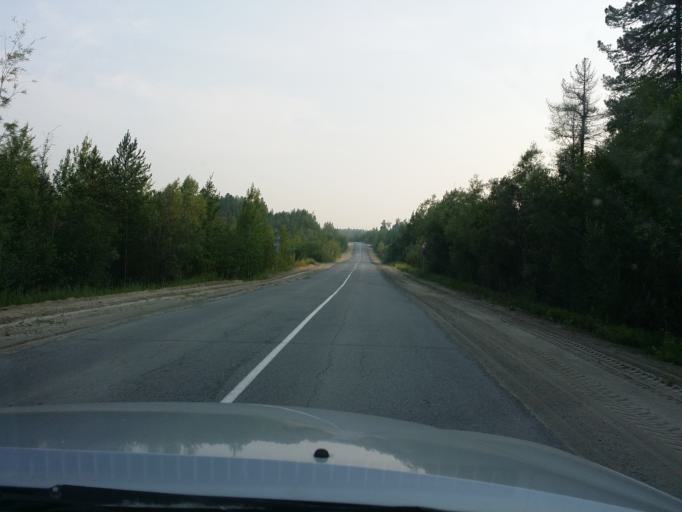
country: RU
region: Khanty-Mansiyskiy Avtonomnyy Okrug
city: Nizhnevartovsk
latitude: 61.4095
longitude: 76.5974
